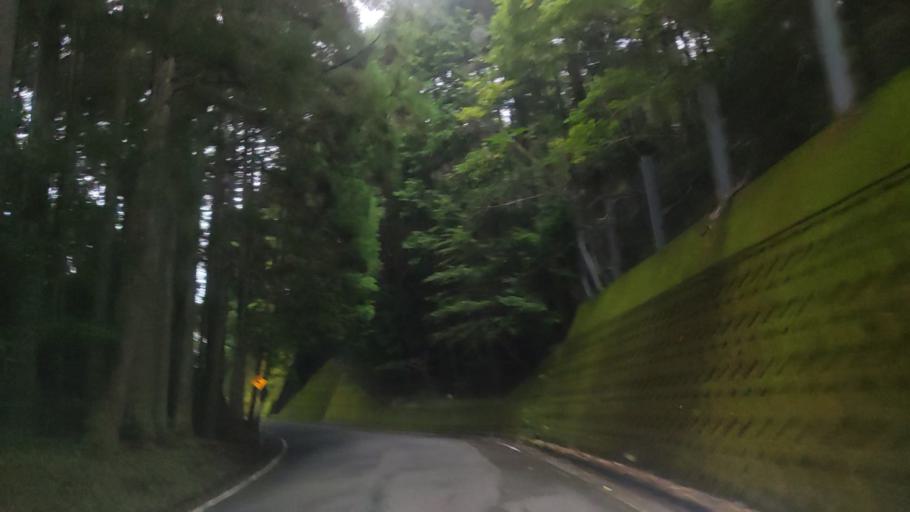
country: JP
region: Wakayama
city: Hashimoto
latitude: 34.2940
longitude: 135.6292
